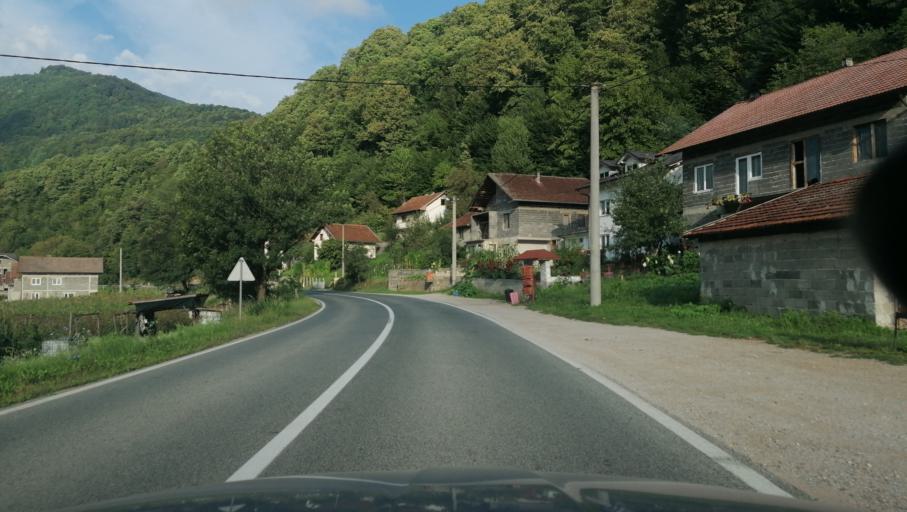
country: BA
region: Federation of Bosnia and Herzegovina
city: Jajce
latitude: 44.2329
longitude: 17.3093
